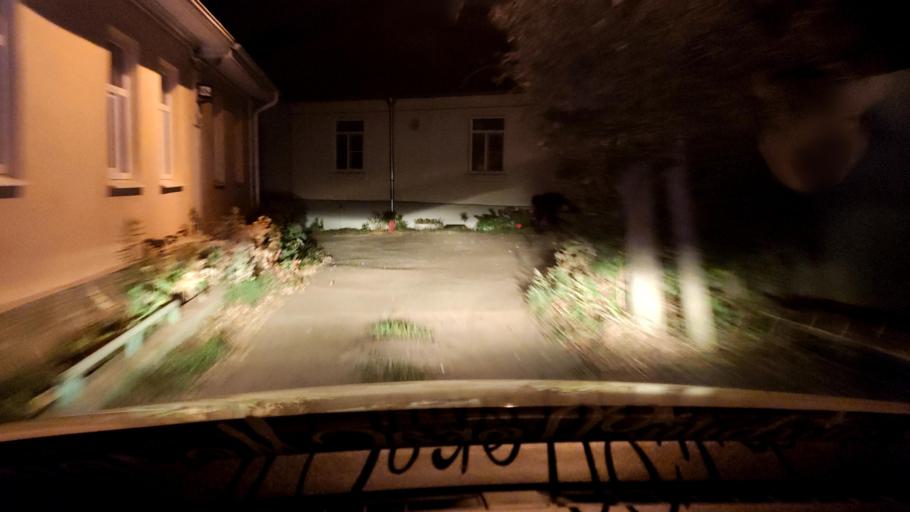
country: RU
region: Voronezj
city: Voronezh
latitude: 51.6909
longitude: 39.2312
